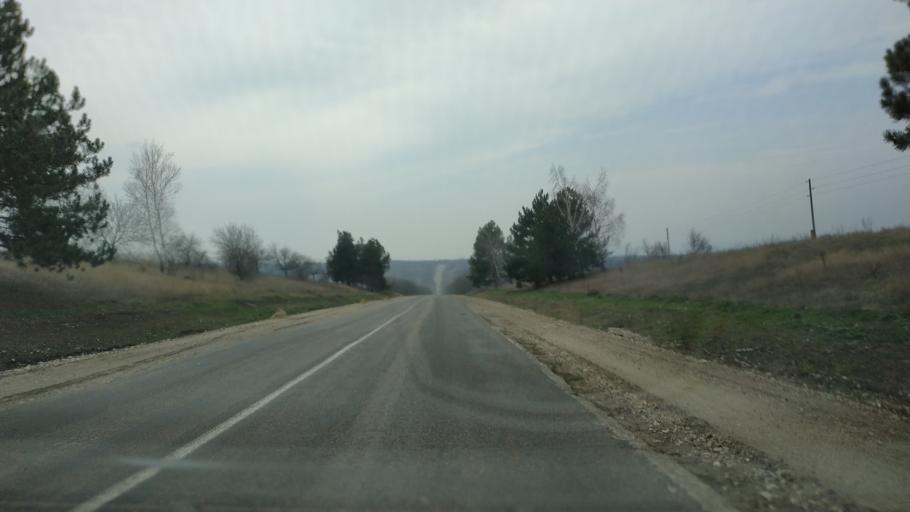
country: MD
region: Cahul
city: Cahul
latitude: 45.9308
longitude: 28.2722
